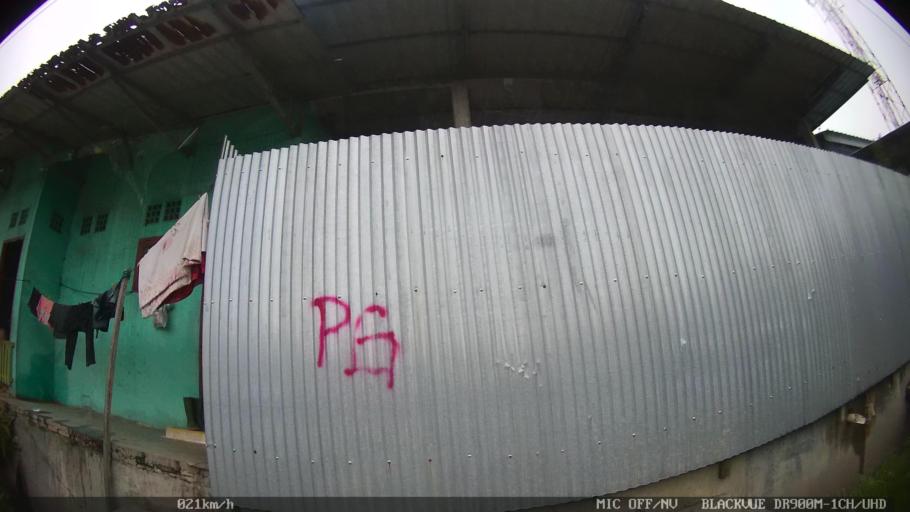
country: ID
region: North Sumatra
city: Deli Tua
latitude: 3.5468
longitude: 98.7156
